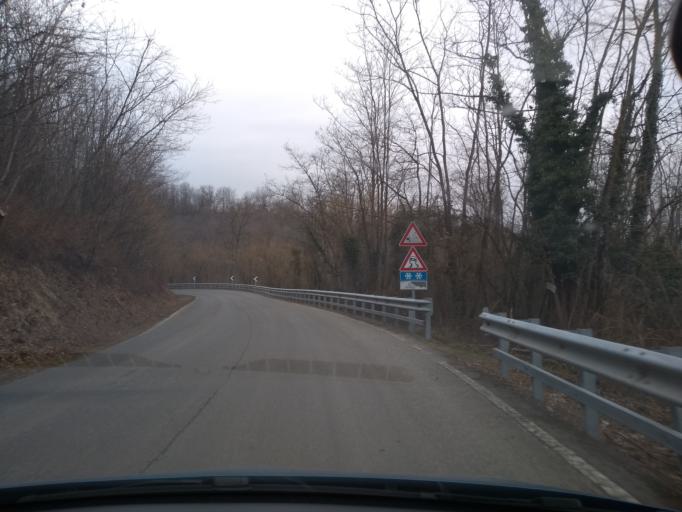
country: IT
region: Piedmont
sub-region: Provincia di Biella
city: Zubiena
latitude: 45.4891
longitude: 7.9881
